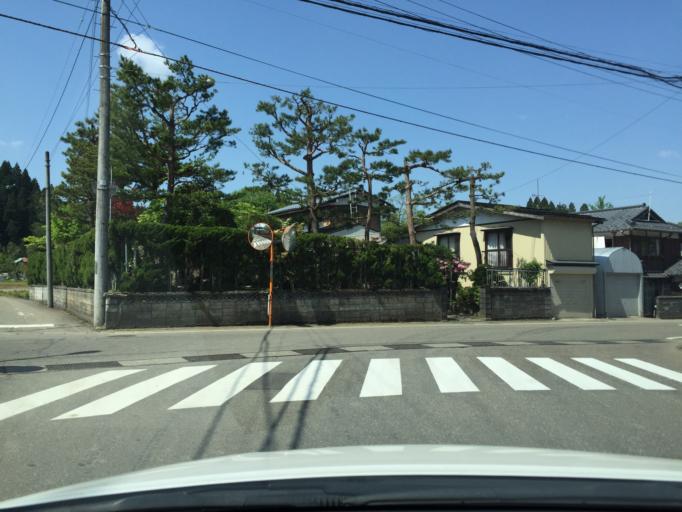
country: JP
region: Niigata
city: Tochio-honcho
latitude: 37.5046
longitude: 139.0562
